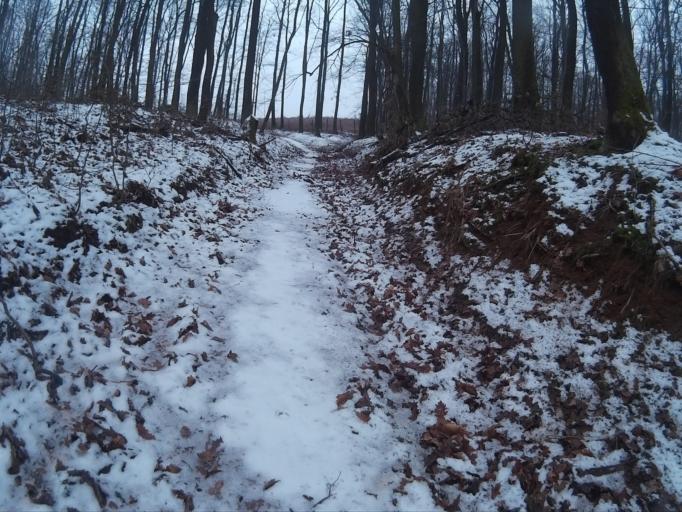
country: HU
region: Komarom-Esztergom
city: Tarjan
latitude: 47.5905
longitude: 18.5124
